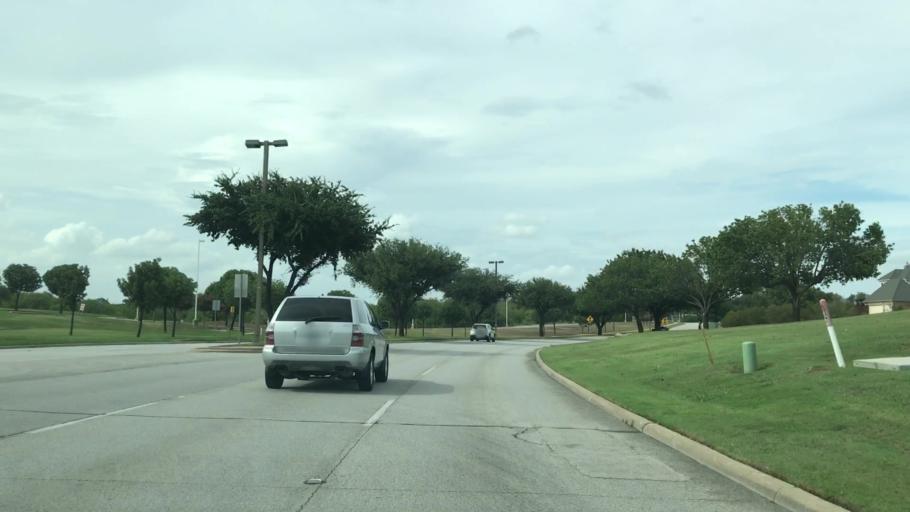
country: US
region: Texas
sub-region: Dallas County
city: Irving
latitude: 32.8673
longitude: -96.9599
